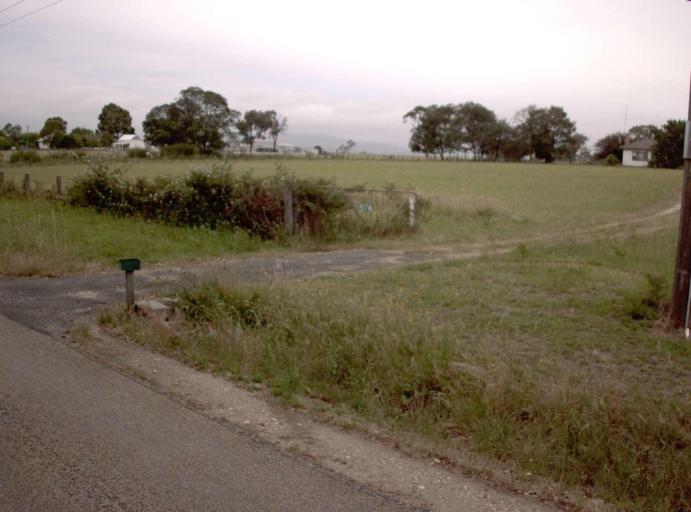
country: AU
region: Victoria
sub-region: East Gippsland
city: Bairnsdale
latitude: -37.8302
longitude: 147.4335
